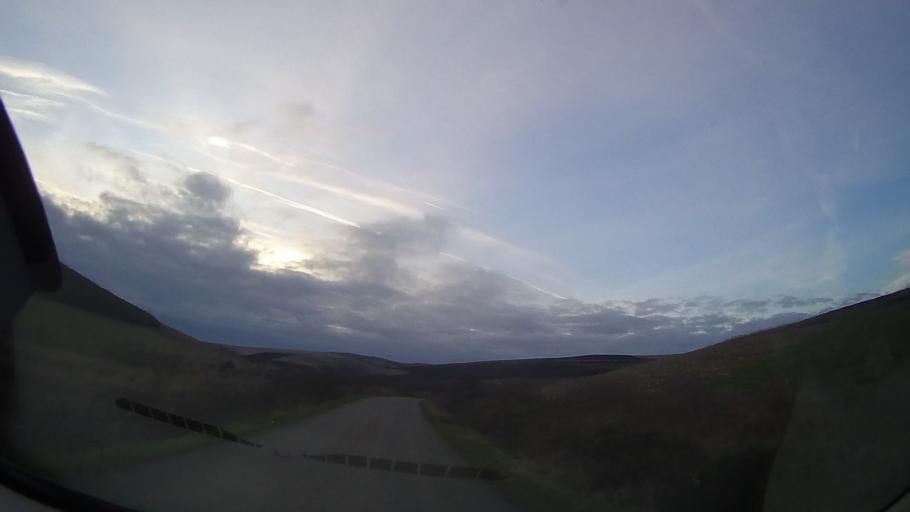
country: RO
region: Cluj
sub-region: Comuna Geaca
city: Geaca
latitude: 46.8529
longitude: 24.0728
